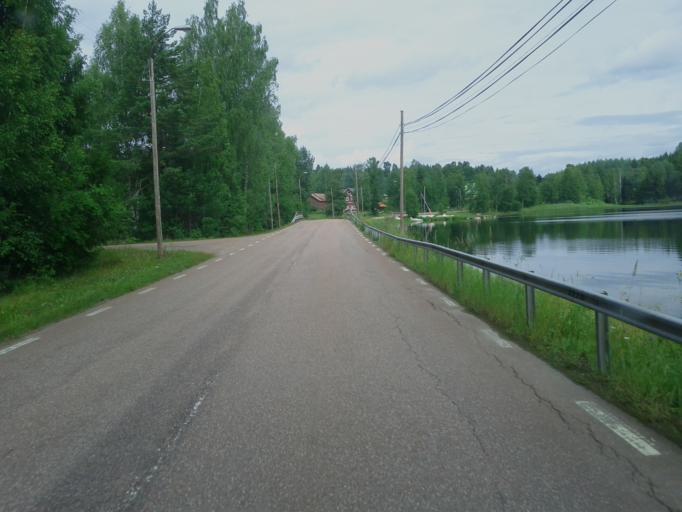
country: SE
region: Dalarna
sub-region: Smedjebackens Kommun
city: Smedjebacken
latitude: 60.3107
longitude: 15.3733
